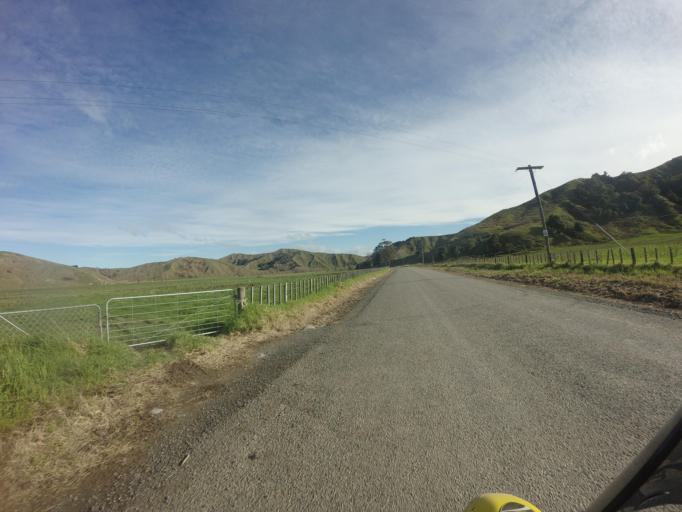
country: NZ
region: Hawke's Bay
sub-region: Wairoa District
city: Wairoa
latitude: -39.0272
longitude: 177.5821
